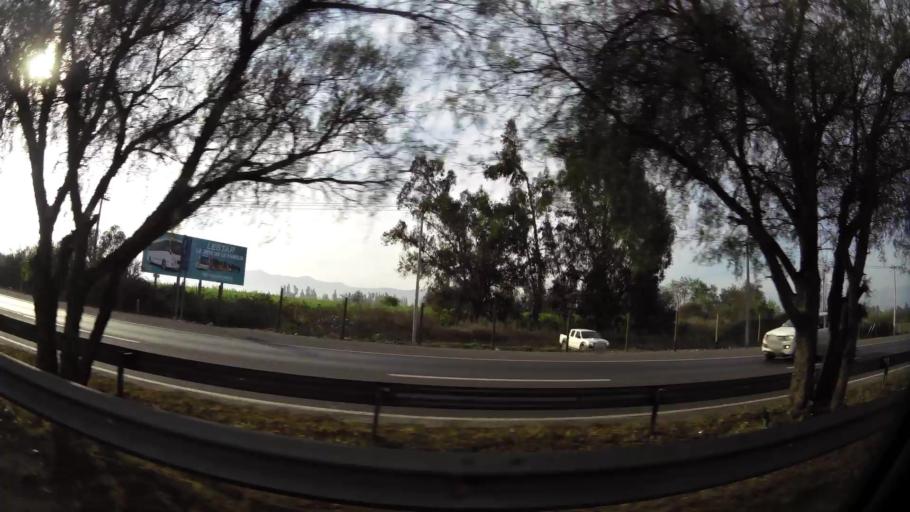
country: CL
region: Santiago Metropolitan
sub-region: Provincia de Talagante
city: Penaflor
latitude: -33.6498
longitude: -70.8808
